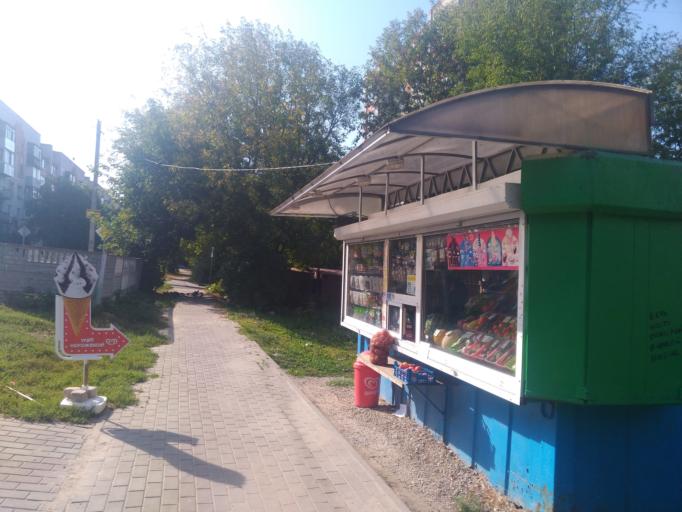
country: RU
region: Kaluga
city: Kaluga
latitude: 54.5319
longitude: 36.2534
